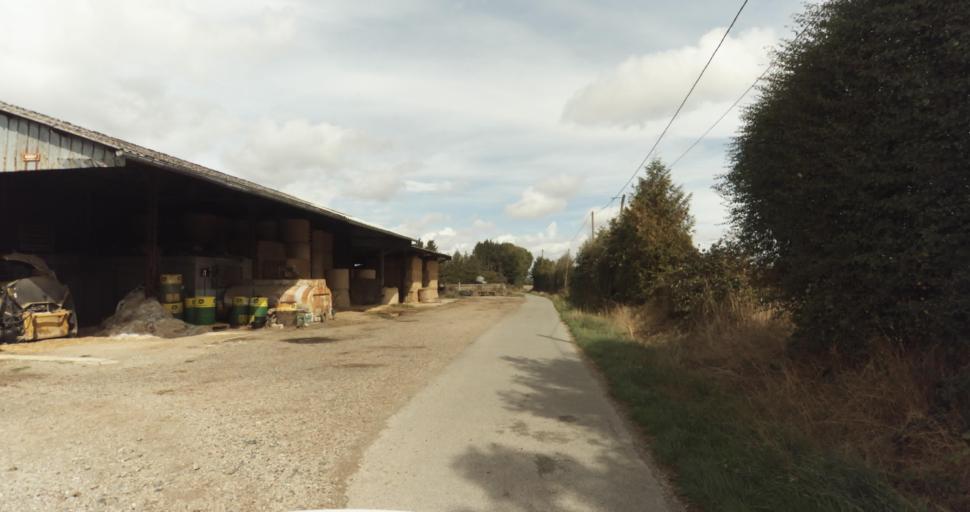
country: FR
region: Lower Normandy
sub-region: Departement de l'Orne
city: Gace
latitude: 48.7988
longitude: 0.3709
